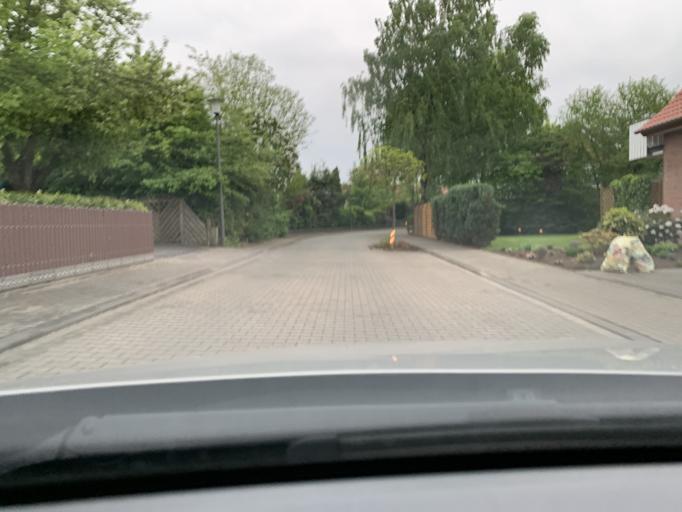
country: DE
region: North Rhine-Westphalia
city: Rietberg
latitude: 51.8011
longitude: 8.3732
